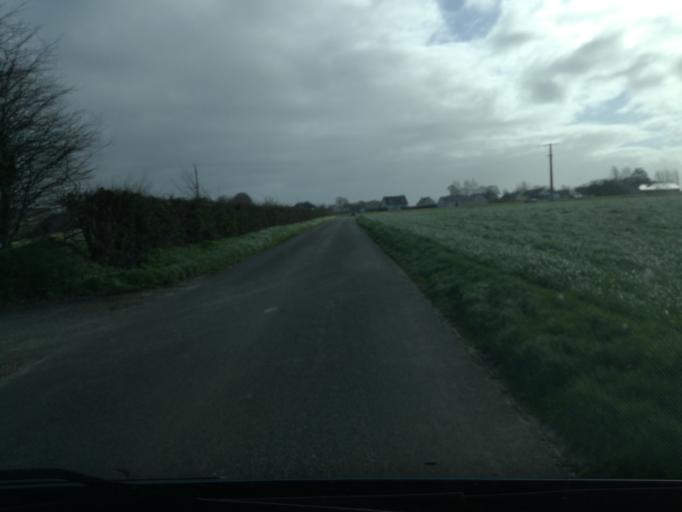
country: FR
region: Haute-Normandie
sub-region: Departement de la Seine-Maritime
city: Yport
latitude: 49.7380
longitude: 0.3282
